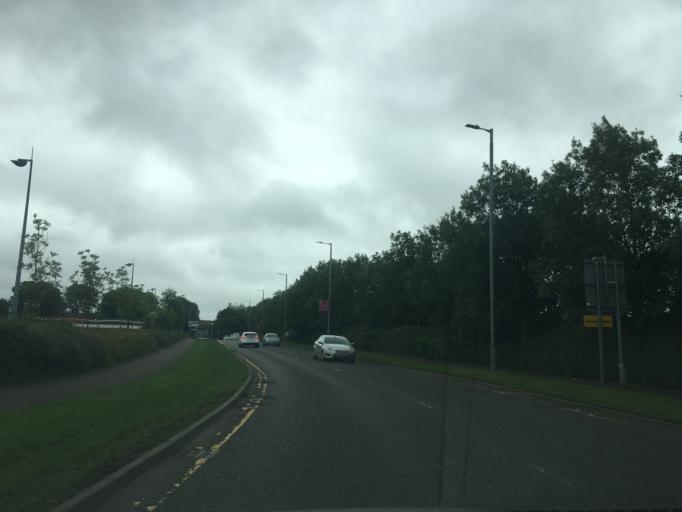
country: GB
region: Scotland
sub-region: Renfrewshire
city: Renfrew
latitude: 55.8722
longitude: -4.3592
